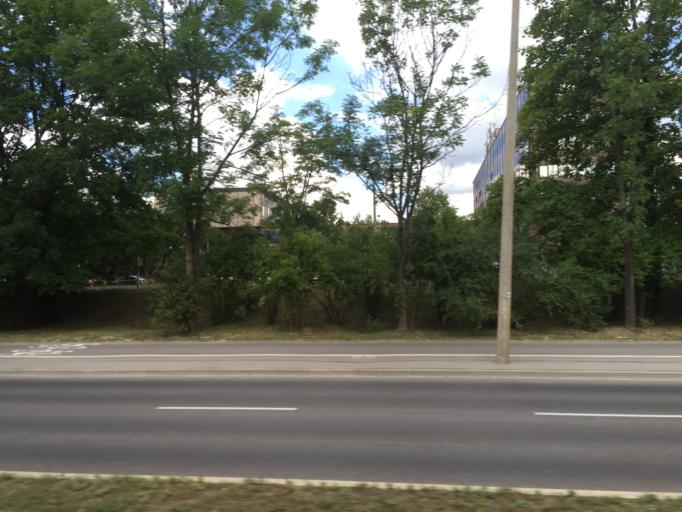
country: PL
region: Lesser Poland Voivodeship
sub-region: Krakow
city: Krakow
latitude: 50.0739
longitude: 19.9973
